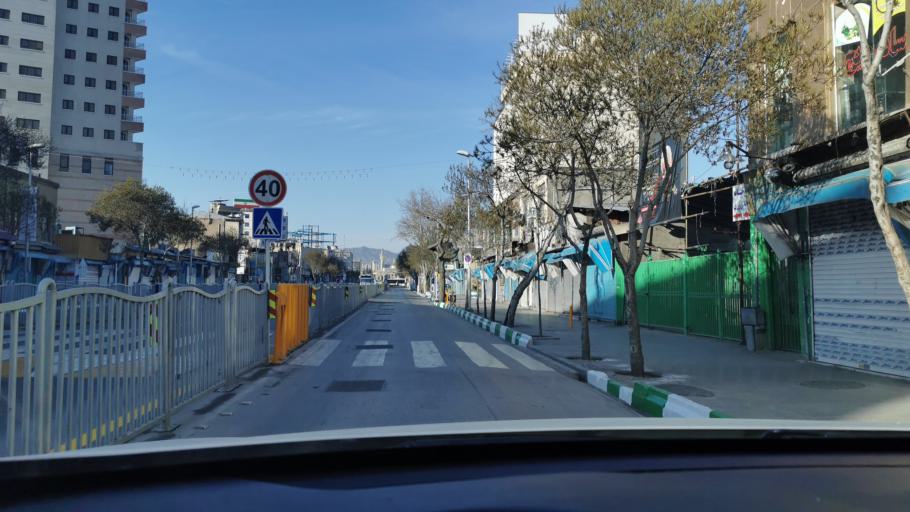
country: IR
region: Razavi Khorasan
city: Mashhad
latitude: 36.2933
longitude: 59.6240
